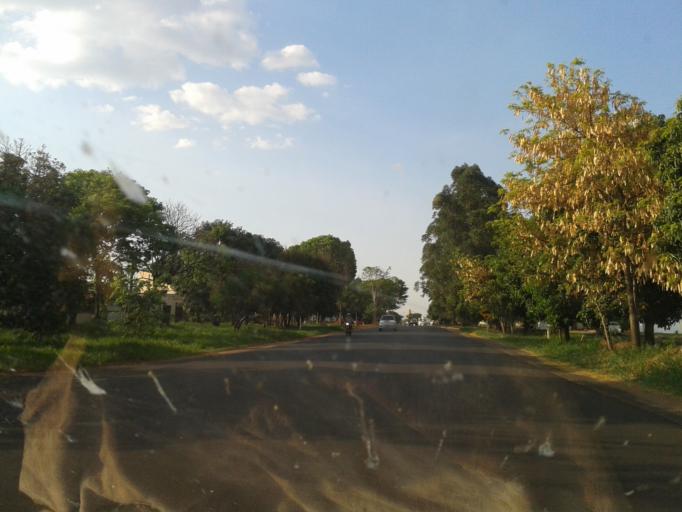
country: BR
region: Minas Gerais
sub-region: Uberlandia
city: Uberlandia
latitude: -18.9436
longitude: -48.3072
